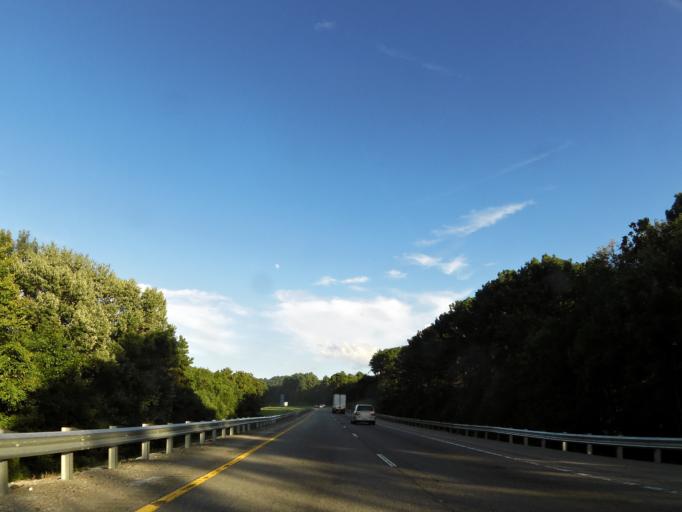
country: US
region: Tennessee
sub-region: Smith County
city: Gordonsville
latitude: 36.1498
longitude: -85.8727
